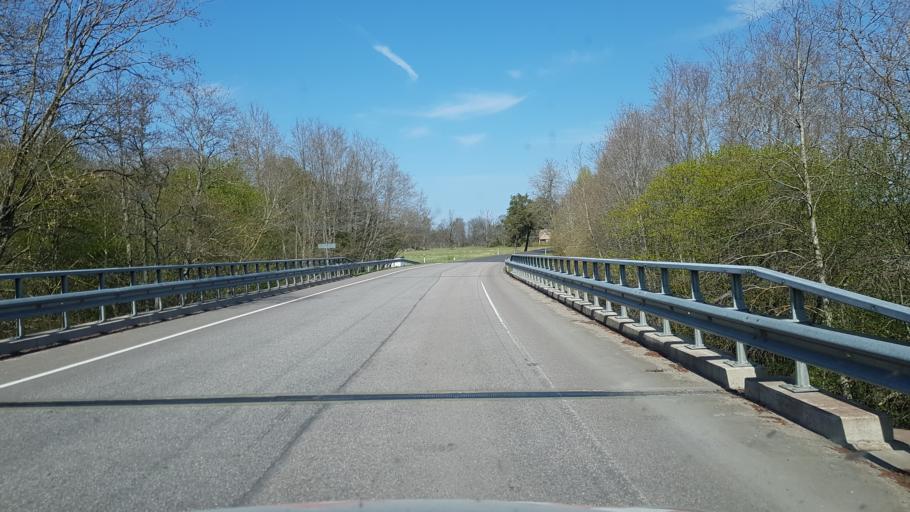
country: EE
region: Harju
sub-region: Keila linn
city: Keila
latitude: 59.4118
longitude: 24.4113
